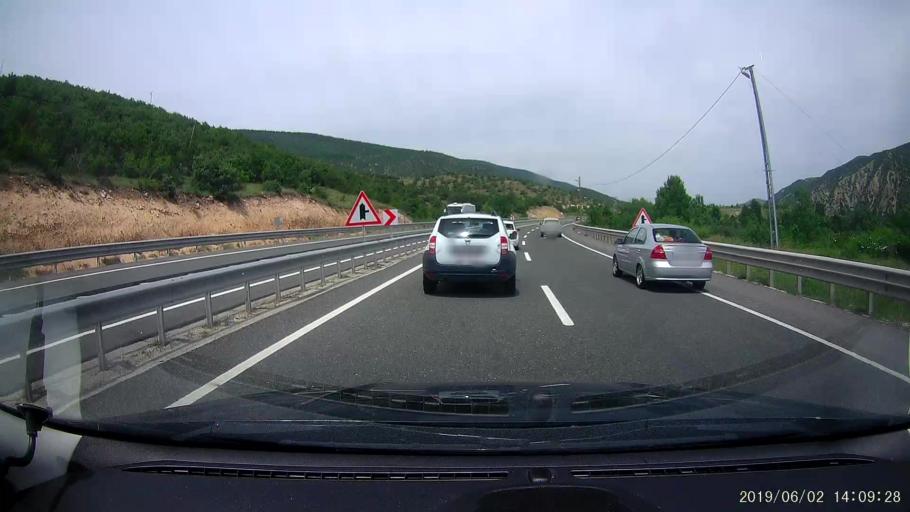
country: TR
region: Cankiri
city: Ilgaz
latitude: 40.8949
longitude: 33.7422
